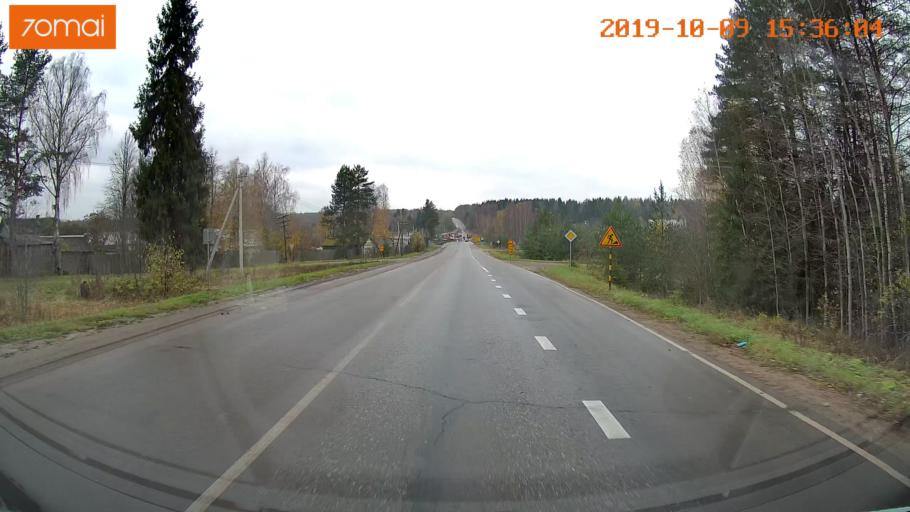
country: RU
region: Kostroma
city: Oktyabr'skiy
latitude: 57.9261
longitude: 41.2151
